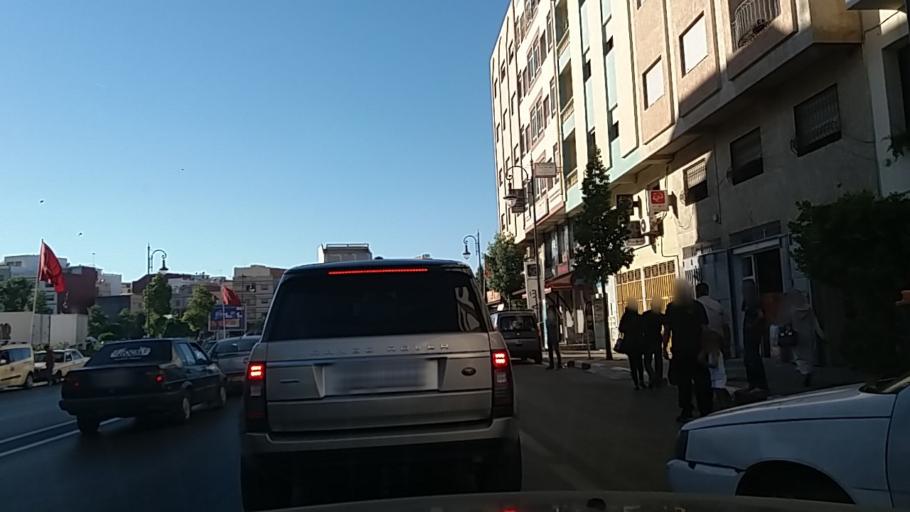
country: MA
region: Tanger-Tetouan
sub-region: Tanger-Assilah
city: Tangier
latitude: 35.7511
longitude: -5.7996
